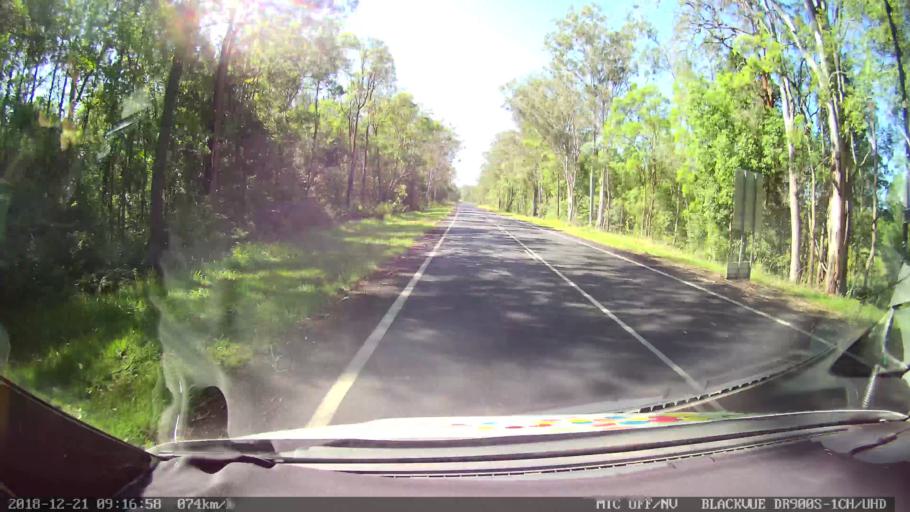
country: AU
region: New South Wales
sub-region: Clarence Valley
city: Maclean
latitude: -29.2874
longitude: 152.9891
